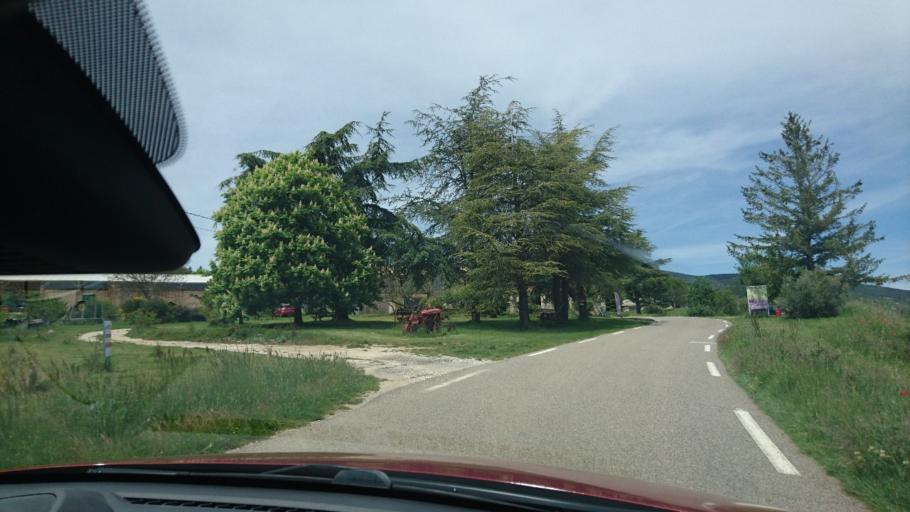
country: FR
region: Provence-Alpes-Cote d'Azur
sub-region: Departement du Vaucluse
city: Sault
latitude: 44.1133
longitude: 5.3973
